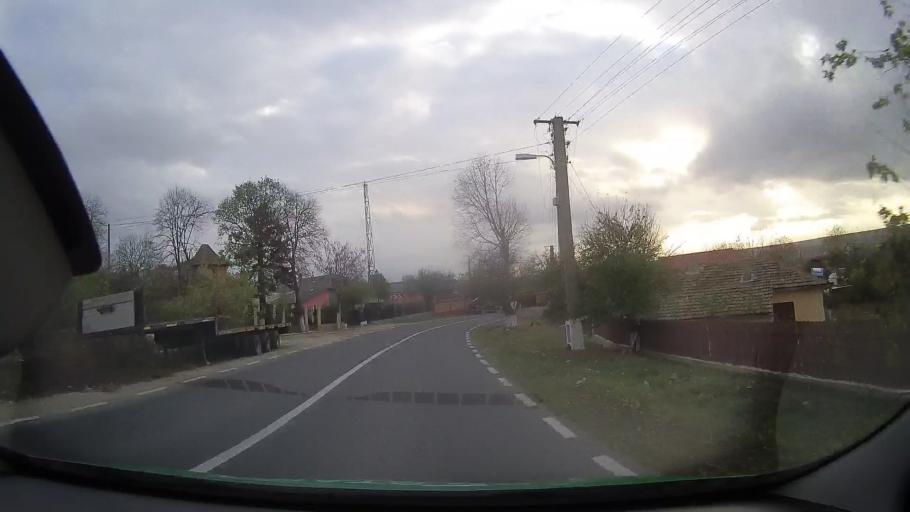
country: RO
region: Constanta
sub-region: Comuna Adamclisi
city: Adamclisi
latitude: 44.0864
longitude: 27.9607
